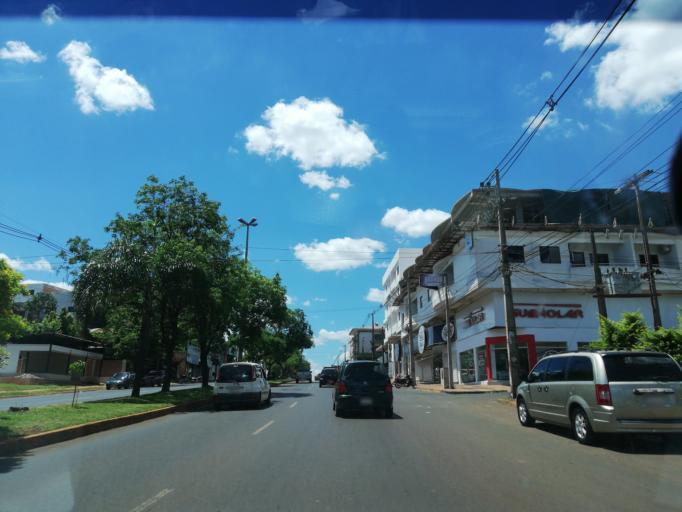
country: PY
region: Itapua
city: Encarnacion
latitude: -27.3429
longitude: -55.8576
